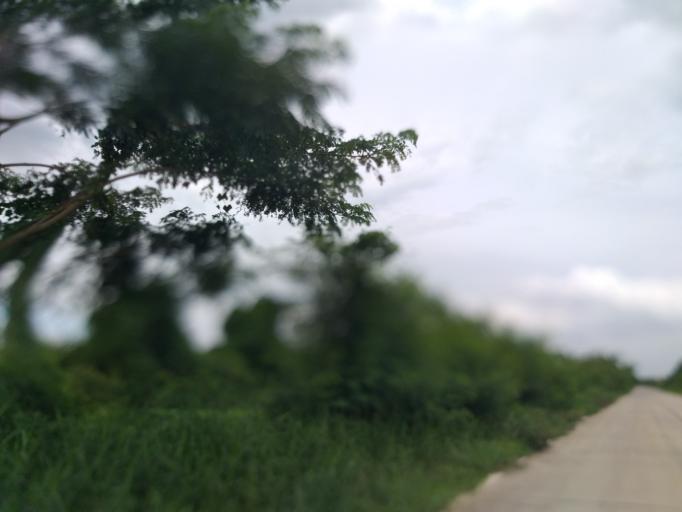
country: TH
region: Pathum Thani
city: Ban Lam Luk Ka
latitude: 13.9673
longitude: 100.8528
